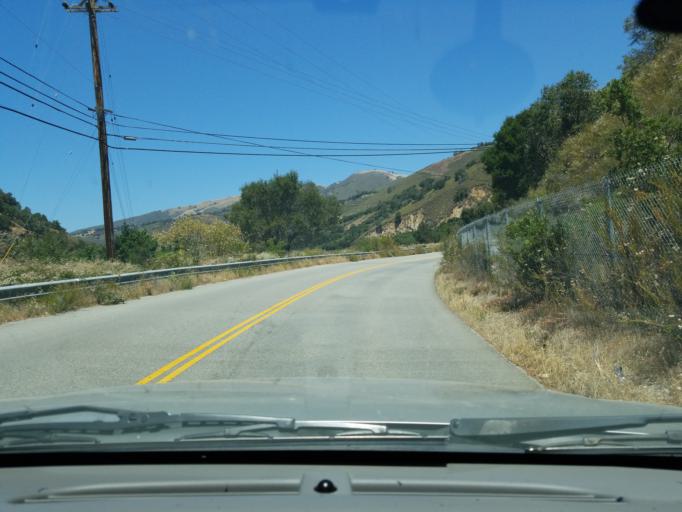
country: US
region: California
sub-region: Monterey County
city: Carmel Valley Village
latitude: 36.4653
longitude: -121.7135
